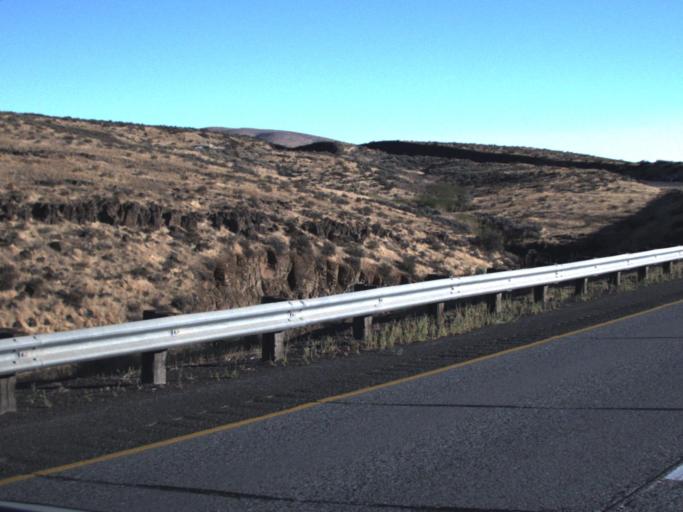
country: US
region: Washington
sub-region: Kittitas County
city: Kittitas
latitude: 46.8092
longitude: -120.3530
